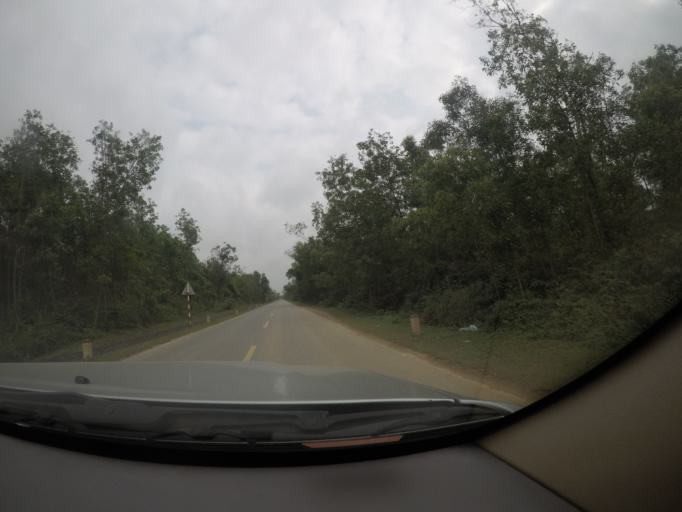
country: VN
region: Quang Binh
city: Quan Hau
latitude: 17.4094
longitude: 106.6022
